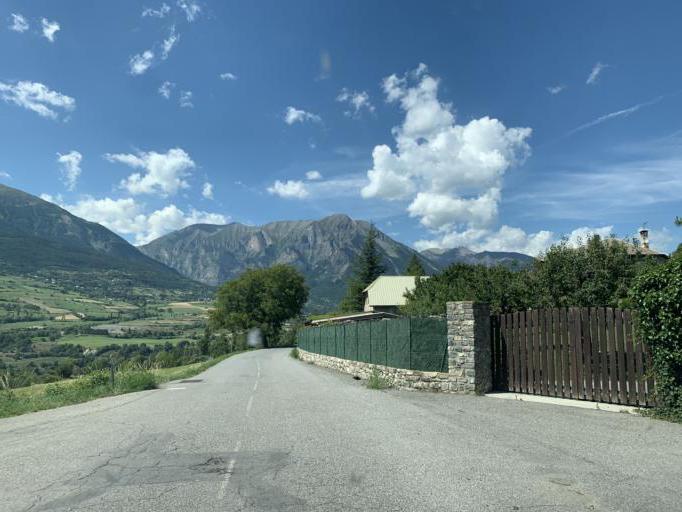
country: FR
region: Provence-Alpes-Cote d'Azur
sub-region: Departement des Hautes-Alpes
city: Embrun
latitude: 44.5810
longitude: 6.5288
